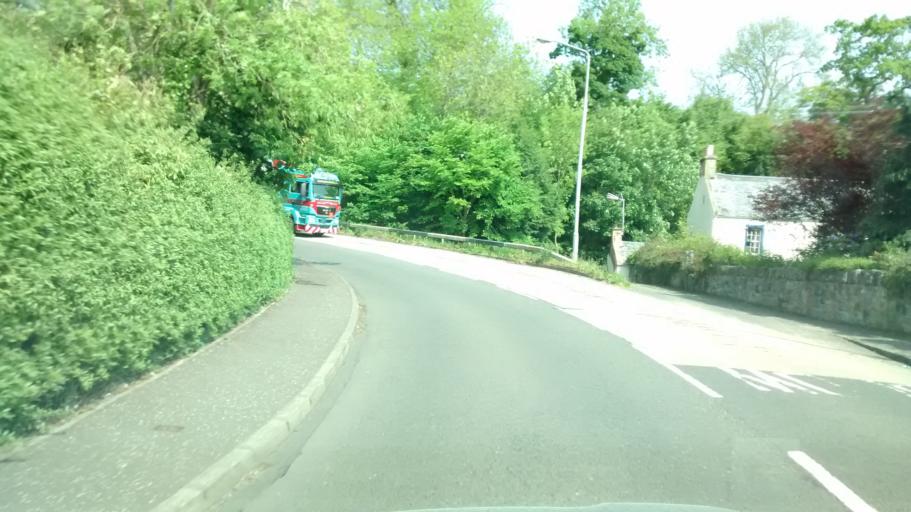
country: GB
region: Scotland
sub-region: West Lothian
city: Mid Calder
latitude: 55.8958
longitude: -3.4785
